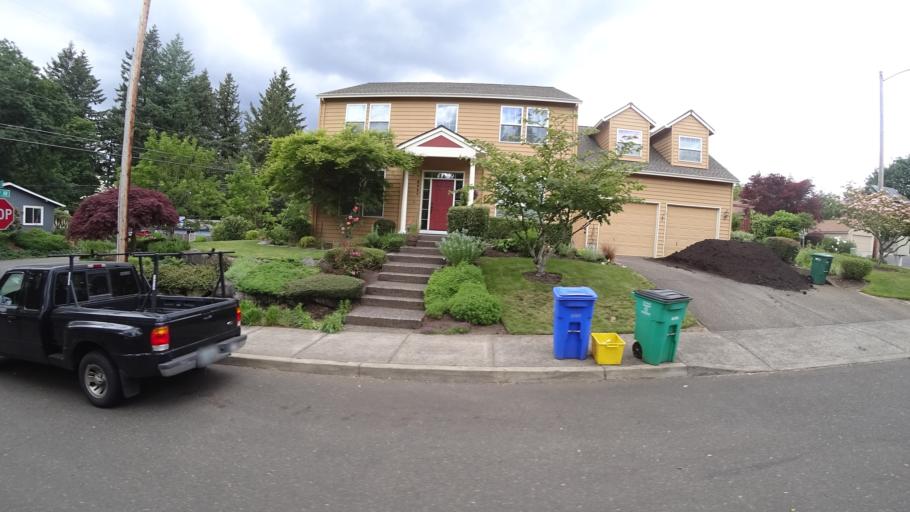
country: US
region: Oregon
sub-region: Clackamas County
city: Lake Oswego
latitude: 45.4514
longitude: -122.7022
